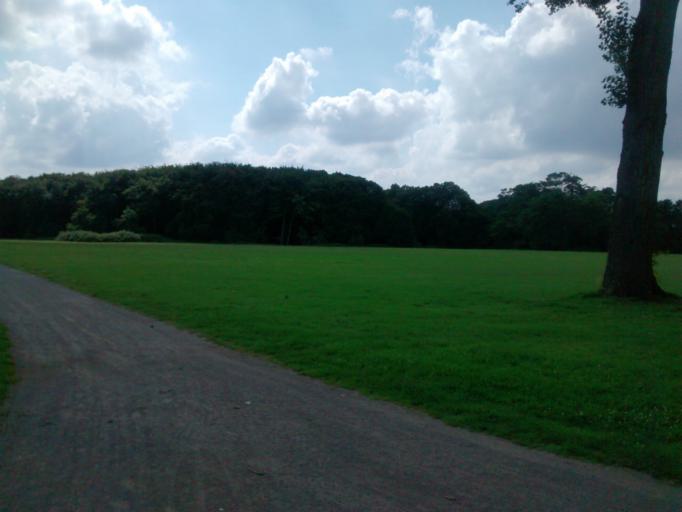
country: DE
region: North Rhine-Westphalia
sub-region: Regierungsbezirk Koln
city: Merheim
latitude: 50.9478
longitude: 7.0367
